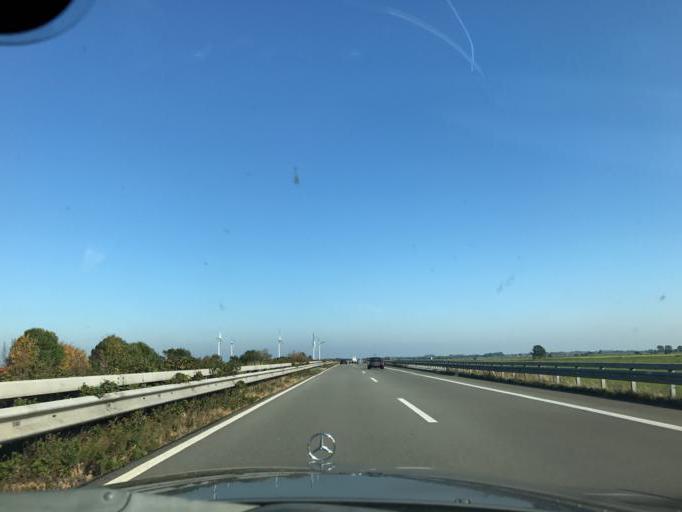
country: DE
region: Lower Saxony
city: Weener
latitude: 53.2160
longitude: 7.3405
